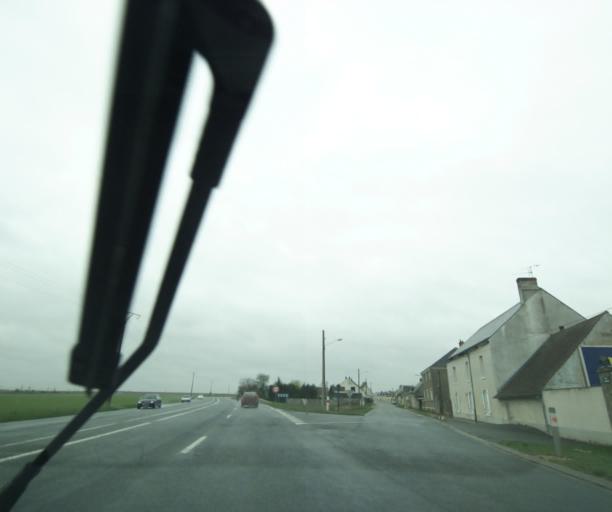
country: FR
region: Centre
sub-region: Departement du Loiret
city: Chevilly
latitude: 48.0528
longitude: 1.8754
